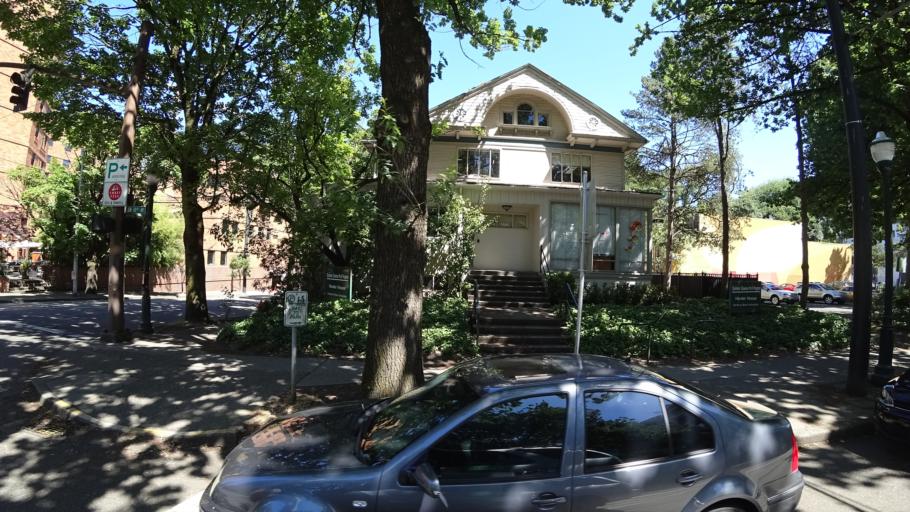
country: US
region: Oregon
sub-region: Multnomah County
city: Portland
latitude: 45.5139
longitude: -122.6854
